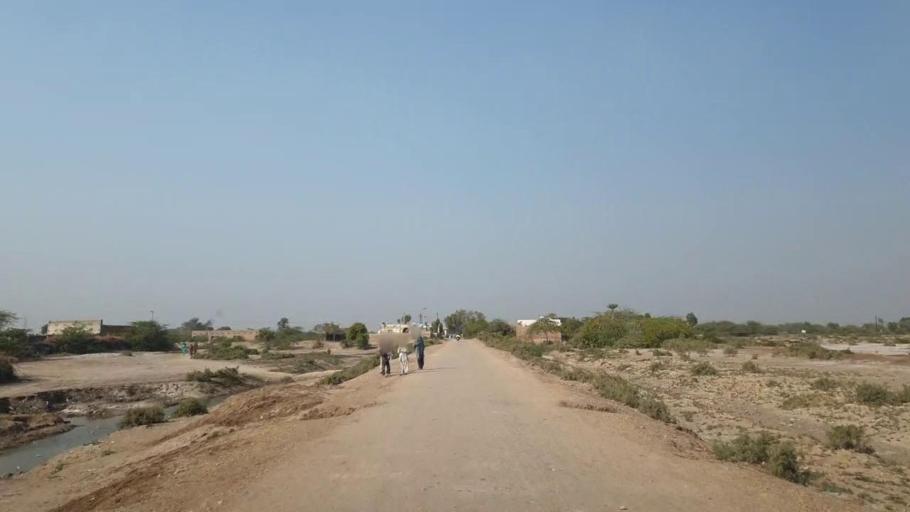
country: PK
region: Sindh
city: Mirpur Khas
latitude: 25.5015
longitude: 68.8848
